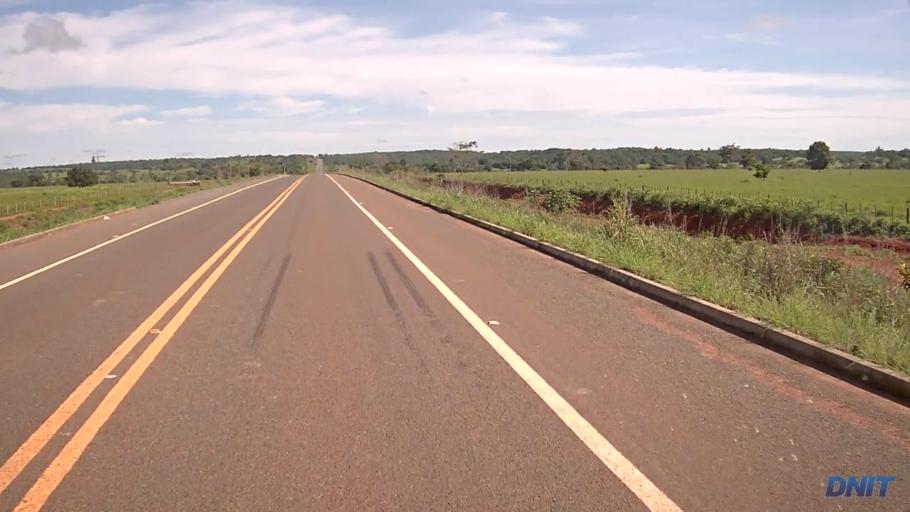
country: BR
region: Goias
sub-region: Sao Miguel Do Araguaia
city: Sao Miguel do Araguaia
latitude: -13.3572
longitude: -50.1476
